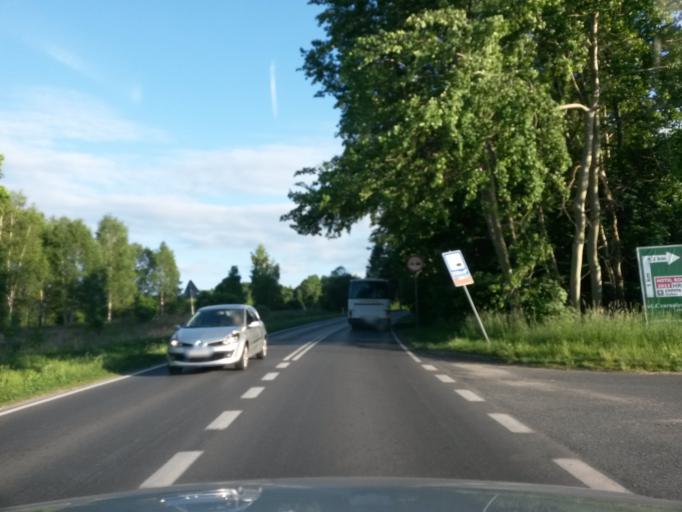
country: PL
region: Lower Silesian Voivodeship
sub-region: Jelenia Gora
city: Jelenia Gora
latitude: 50.8807
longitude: 15.7590
